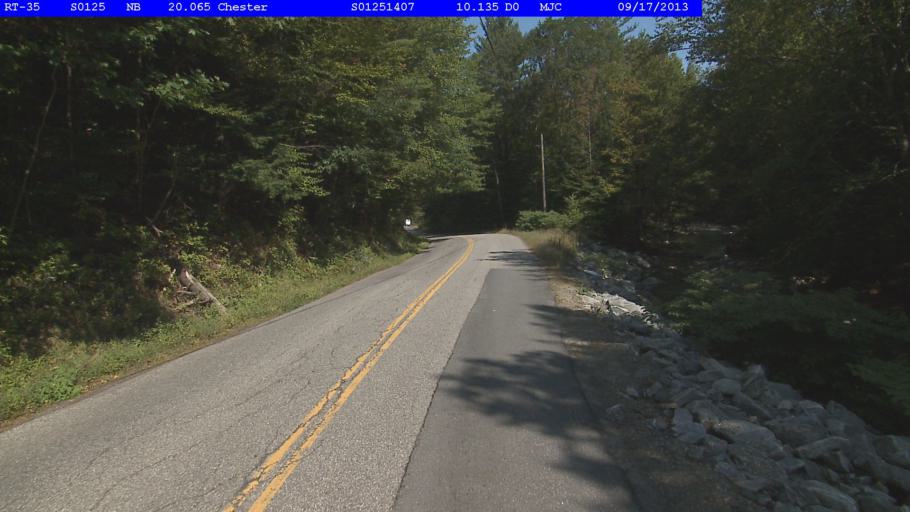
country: US
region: Vermont
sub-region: Windsor County
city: Chester
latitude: 43.2494
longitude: -72.6037
